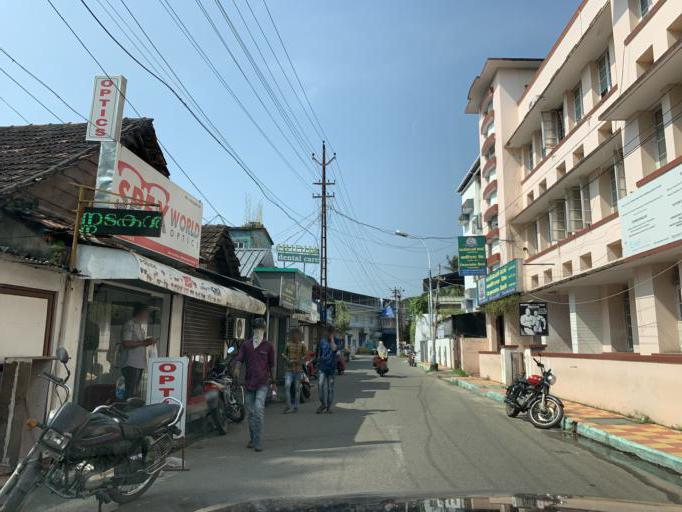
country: IN
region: Kerala
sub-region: Ernakulam
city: Cochin
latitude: 9.9595
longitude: 76.2579
